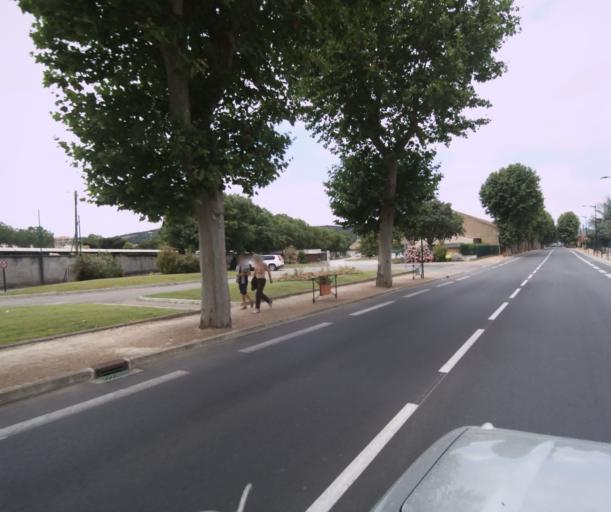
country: FR
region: Languedoc-Roussillon
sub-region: Departement de l'Aude
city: Limoux
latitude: 43.0634
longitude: 2.2157
